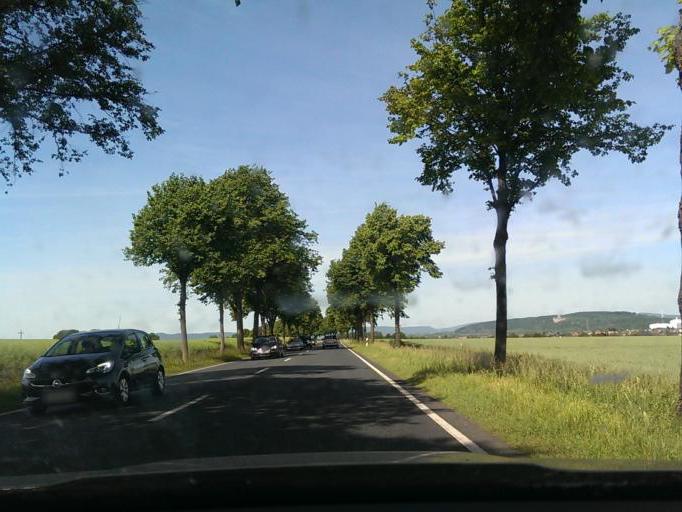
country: DE
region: Lower Saxony
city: Heyersum
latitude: 52.1569
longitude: 9.8262
